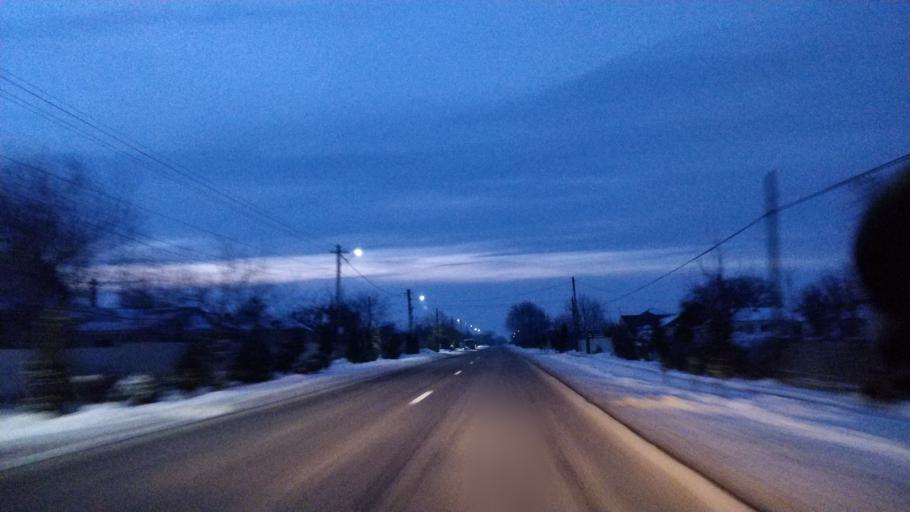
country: RO
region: Vrancea
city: Vulturu de Sus
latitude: 45.6360
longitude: 27.3779
